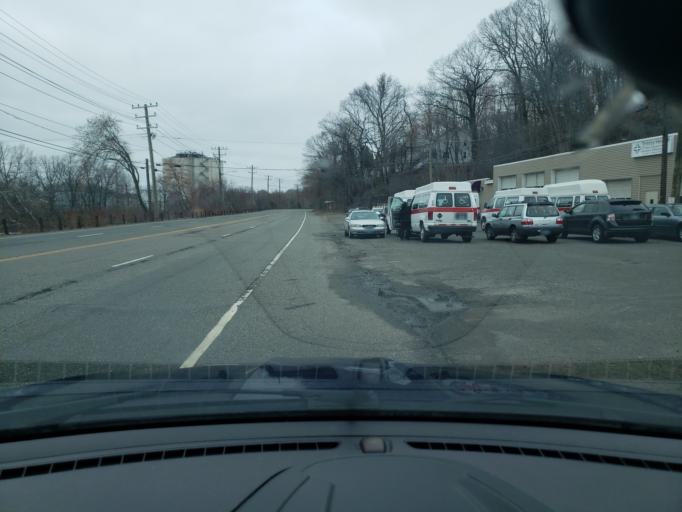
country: US
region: Connecticut
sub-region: New Haven County
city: Waterbury
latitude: 41.5297
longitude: -73.0393
